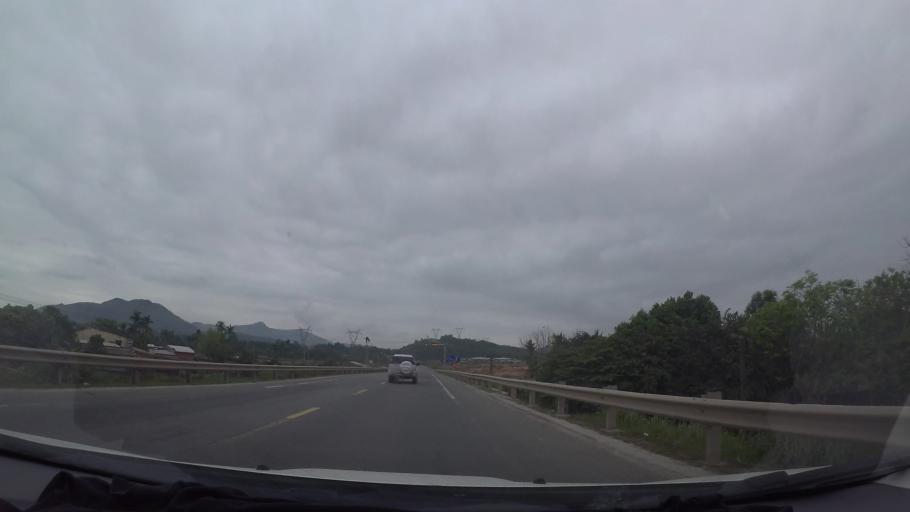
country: VN
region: Da Nang
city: Lien Chieu
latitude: 16.0763
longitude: 108.0872
